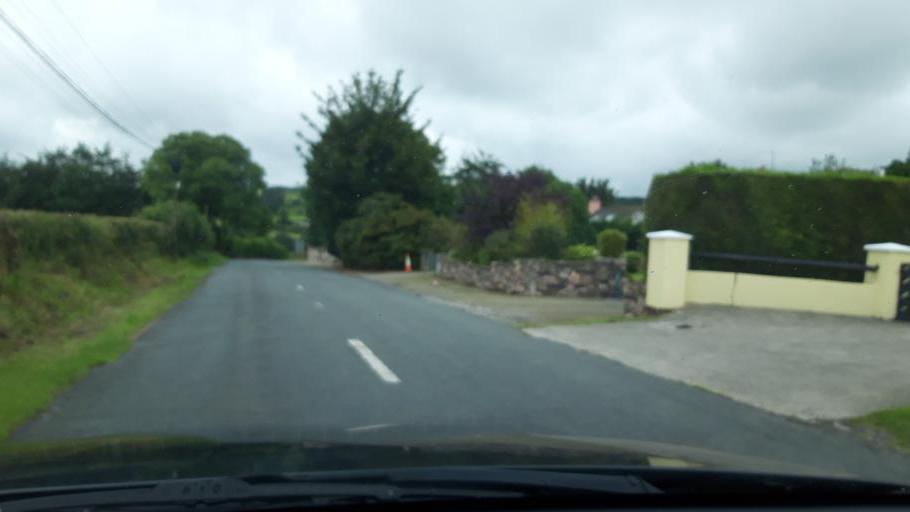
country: IE
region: Munster
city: Cahir
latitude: 52.1756
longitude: -7.8509
